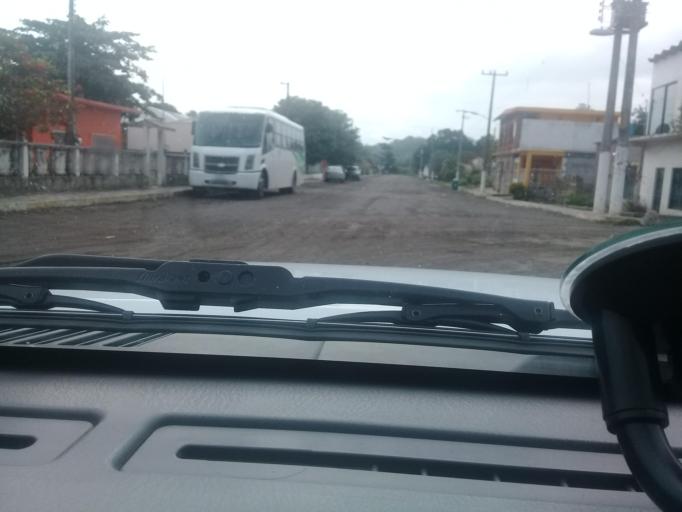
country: MX
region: Veracruz
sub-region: Paso de Ovejas
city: Tolome
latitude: 19.2629
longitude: -96.4114
